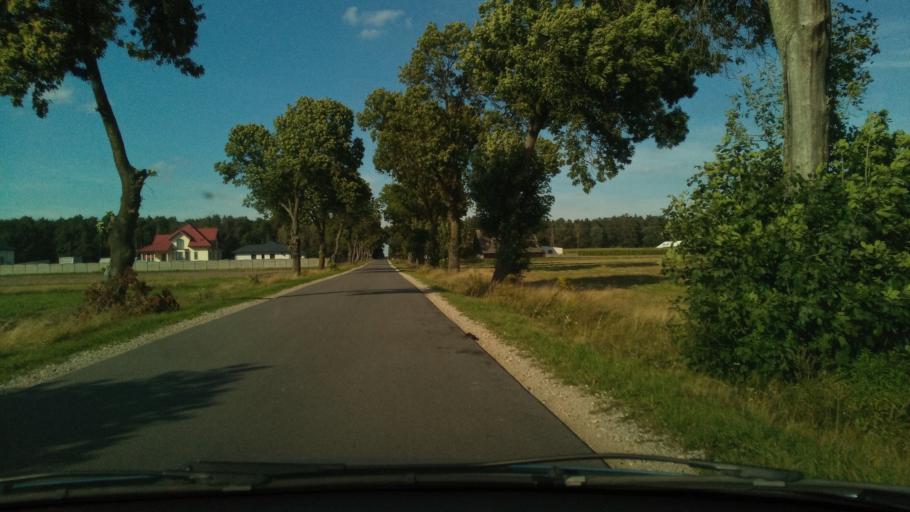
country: PL
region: Lodz Voivodeship
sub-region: Powiat piotrkowski
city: Sulejow
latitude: 51.4046
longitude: 19.8247
